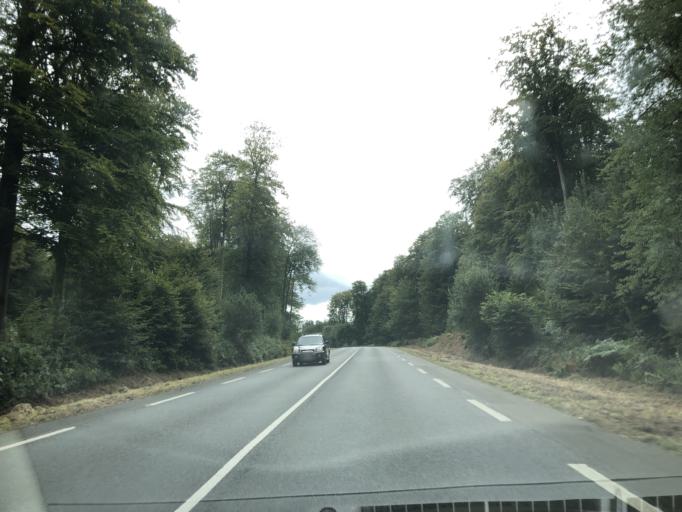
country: FR
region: Nord-Pas-de-Calais
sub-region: Departement du Pas-de-Calais
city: Hesdin
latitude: 50.4051
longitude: 2.0443
